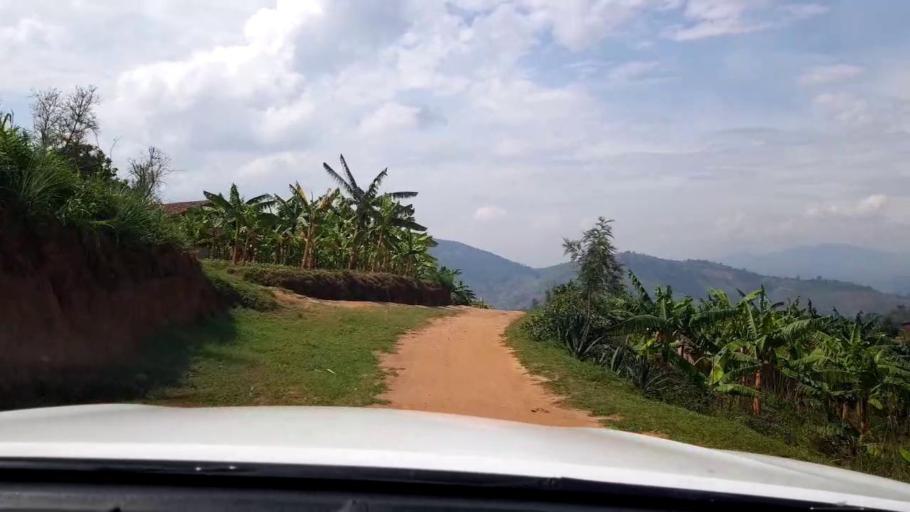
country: RW
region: Southern Province
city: Gitarama
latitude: -2.0566
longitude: 29.6697
